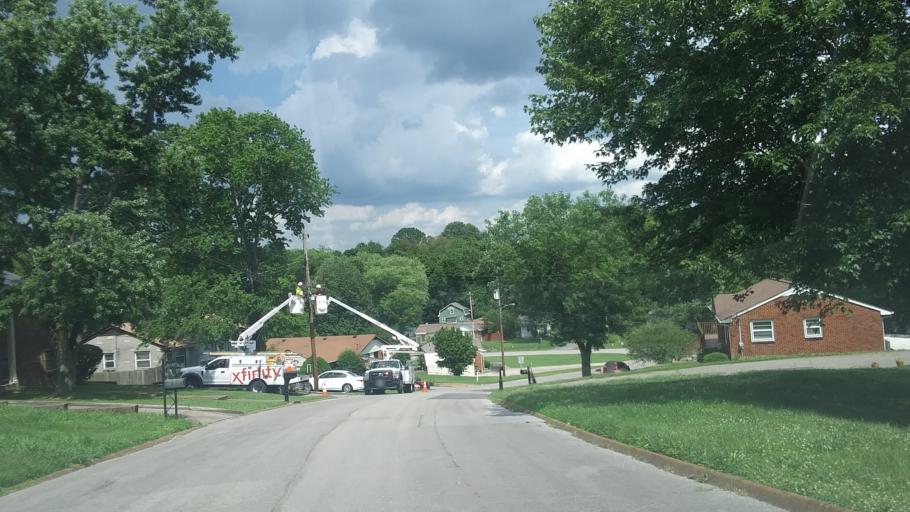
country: US
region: Tennessee
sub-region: Davidson County
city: Oak Hill
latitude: 36.0780
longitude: -86.7067
